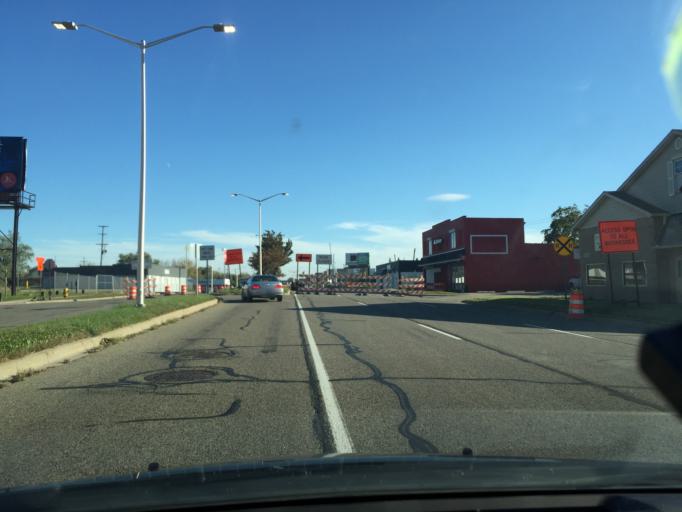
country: US
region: Michigan
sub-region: Oakland County
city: Pontiac
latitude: 42.6246
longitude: -83.2839
